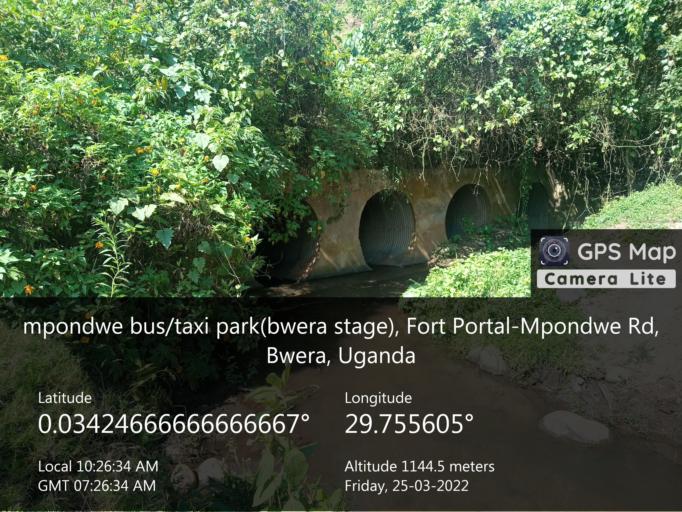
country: UG
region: Western Region
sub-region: Kasese District
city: Kilembe
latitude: 0.0342
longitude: 29.7557
